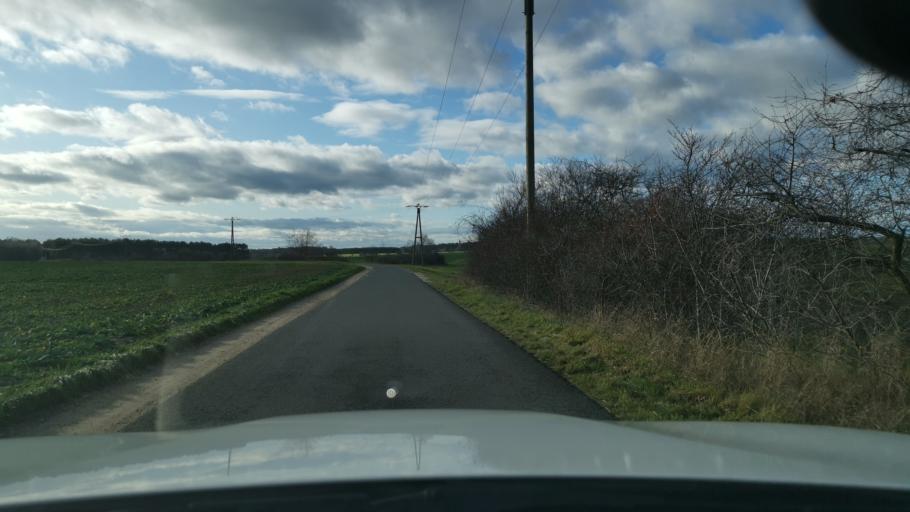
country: DE
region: Saxony-Anhalt
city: Zahna
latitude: 51.8988
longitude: 12.8307
